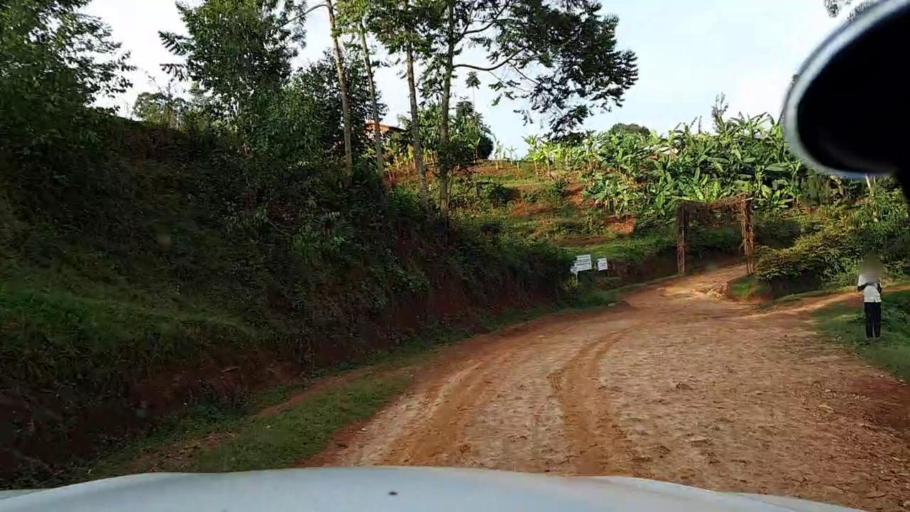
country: RW
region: Southern Province
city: Gitarama
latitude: -2.1856
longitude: 29.5699
